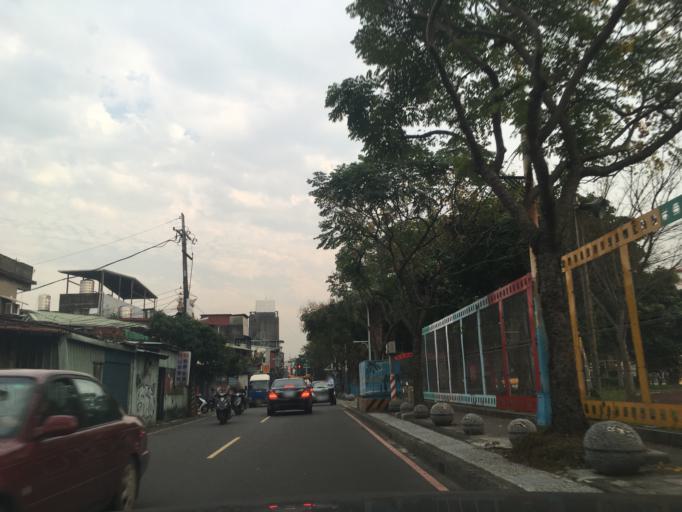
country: TW
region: Taipei
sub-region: Taipei
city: Banqiao
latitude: 25.0100
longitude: 121.4498
